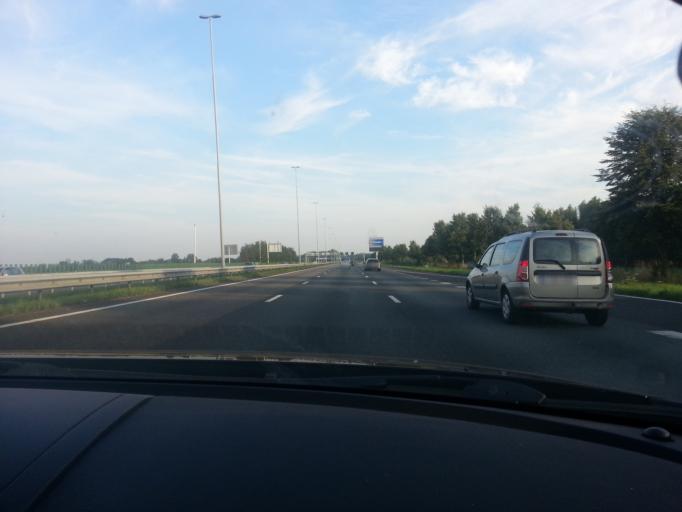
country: NL
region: South Holland
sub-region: Gemeente Delft
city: Delft
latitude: 51.9777
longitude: 4.3969
